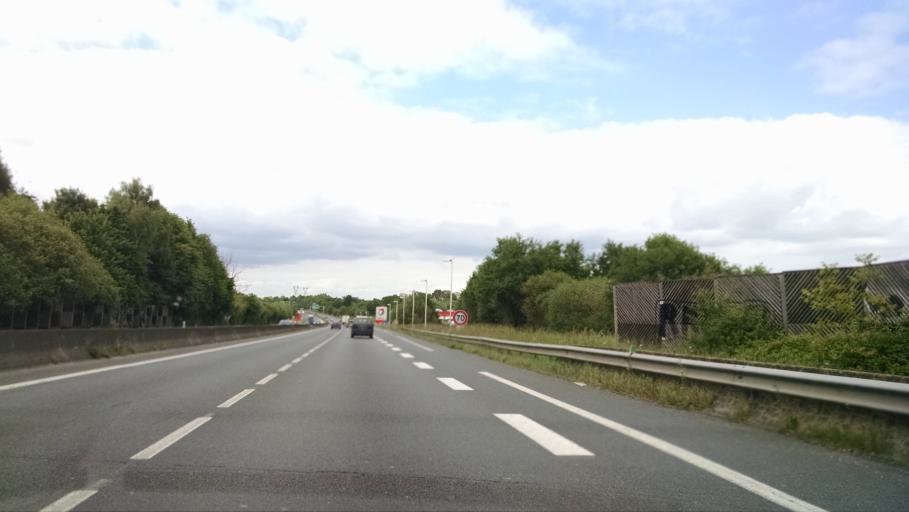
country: FR
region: Pays de la Loire
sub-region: Departement de la Loire-Atlantique
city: Les Sorinieres
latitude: 47.1575
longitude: -1.5133
